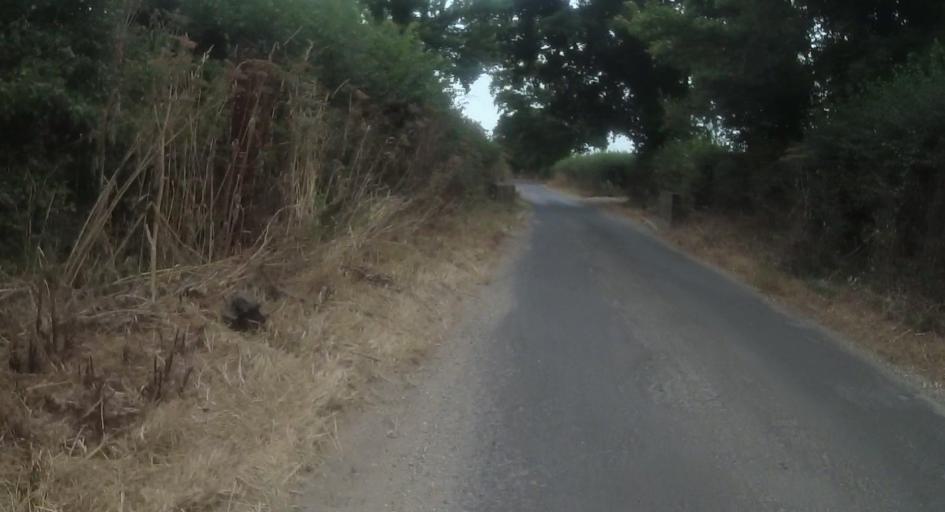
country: GB
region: England
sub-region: Dorset
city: Bovington Camp
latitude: 50.7072
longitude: -2.2884
